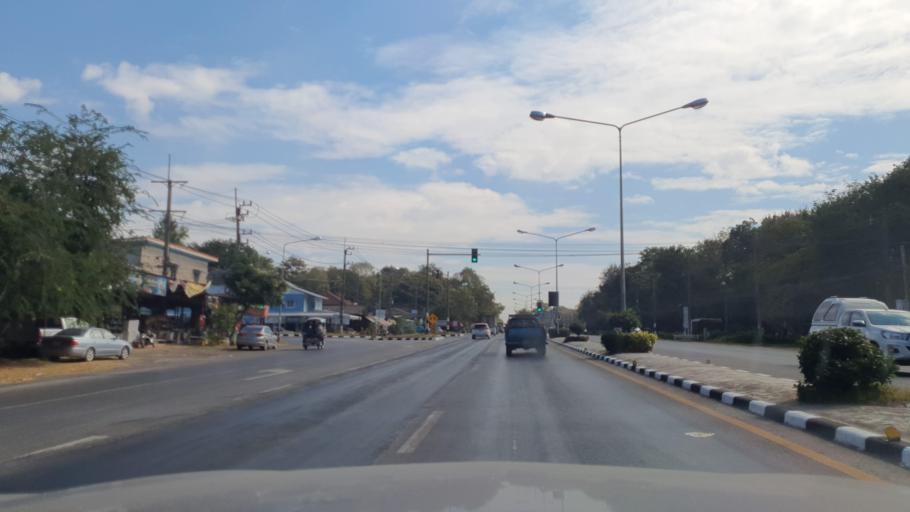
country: TH
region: Kalasin
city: Yang Talat
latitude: 16.4062
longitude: 103.4148
